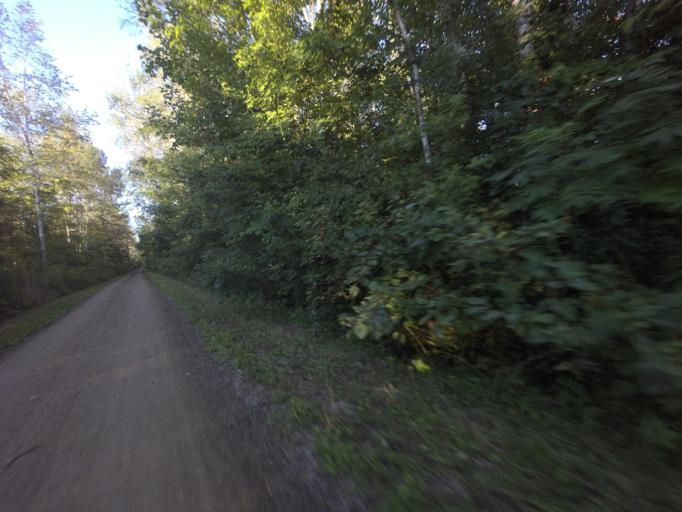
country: CA
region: Ontario
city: Brampton
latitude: 43.8541
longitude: -79.8766
